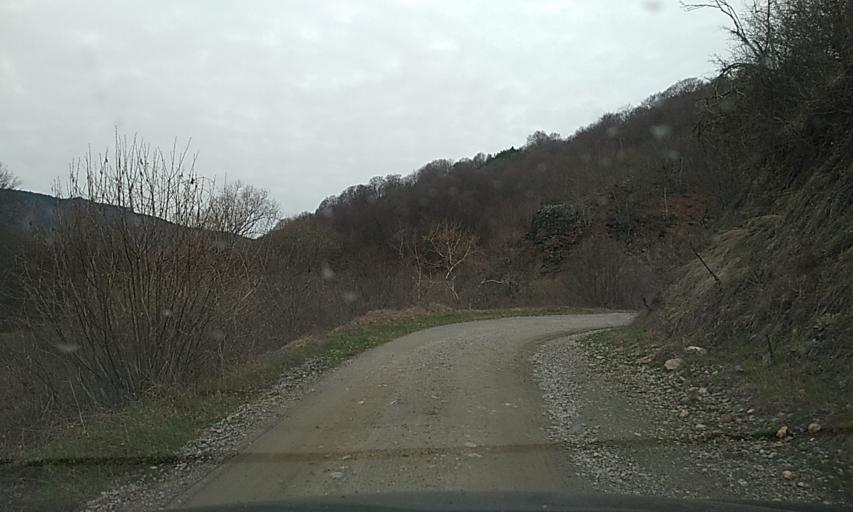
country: MK
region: Kriva Palanka
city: Kriva Palanka
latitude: 42.3418
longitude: 22.3652
